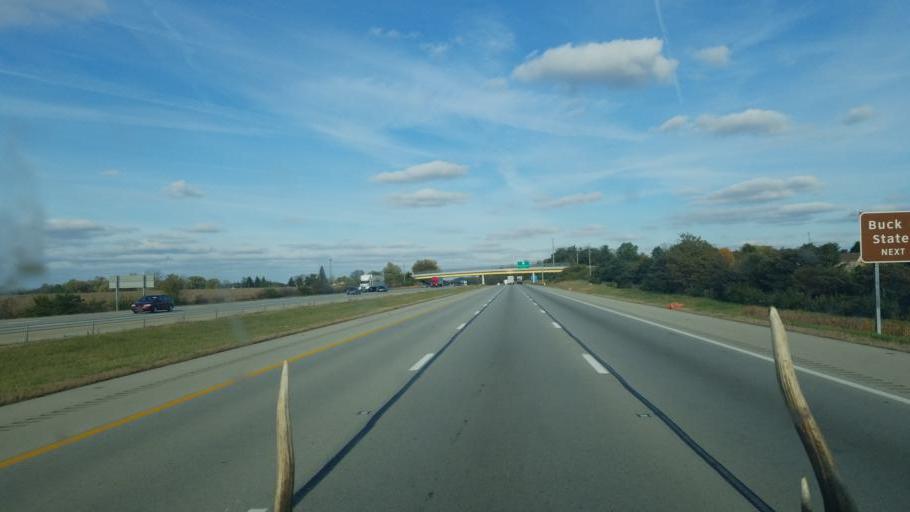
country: US
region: Ohio
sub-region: Clark County
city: Lisbon
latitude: 39.9147
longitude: -83.6988
